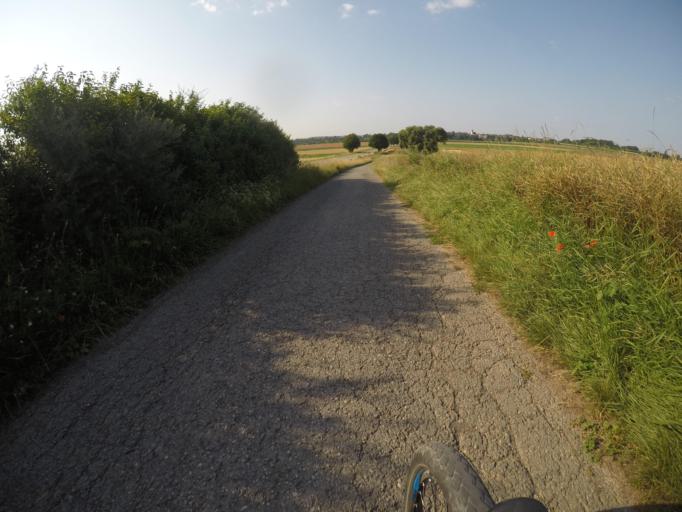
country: DE
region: Baden-Wuerttemberg
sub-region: Regierungsbezirk Stuttgart
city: Herrenberg
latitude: 48.5640
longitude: 8.8799
